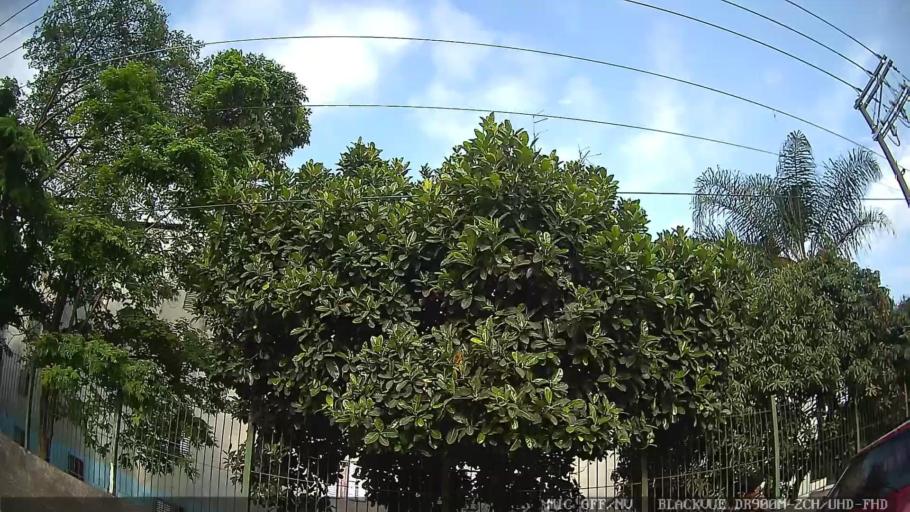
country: BR
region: Sao Paulo
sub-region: Ferraz De Vasconcelos
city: Ferraz de Vasconcelos
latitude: -23.5218
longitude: -46.3996
